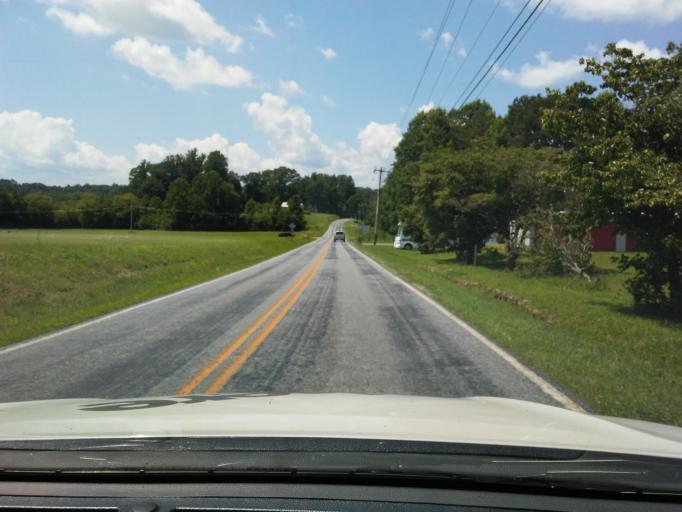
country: US
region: Georgia
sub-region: Towns County
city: Hiawassee
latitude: 34.9919
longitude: -83.7542
